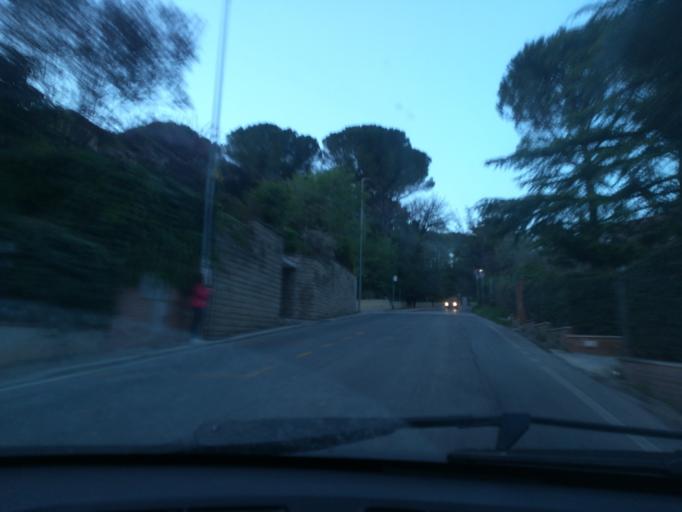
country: IT
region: The Marches
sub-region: Provincia di Macerata
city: Macerata
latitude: 43.2885
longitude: 13.4526
